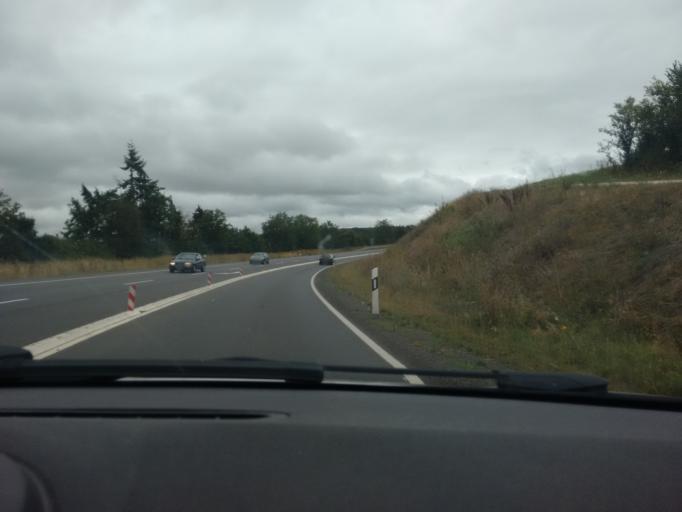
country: DE
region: Rheinland-Pfalz
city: Waldbockelheim
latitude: 49.8172
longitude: 7.7147
